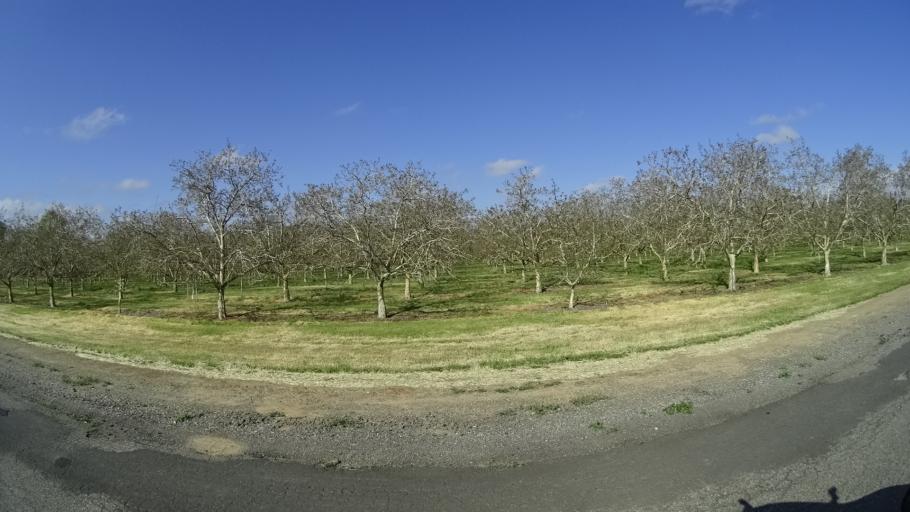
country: US
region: California
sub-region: Butte County
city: Durham
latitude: 39.5091
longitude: -121.9676
